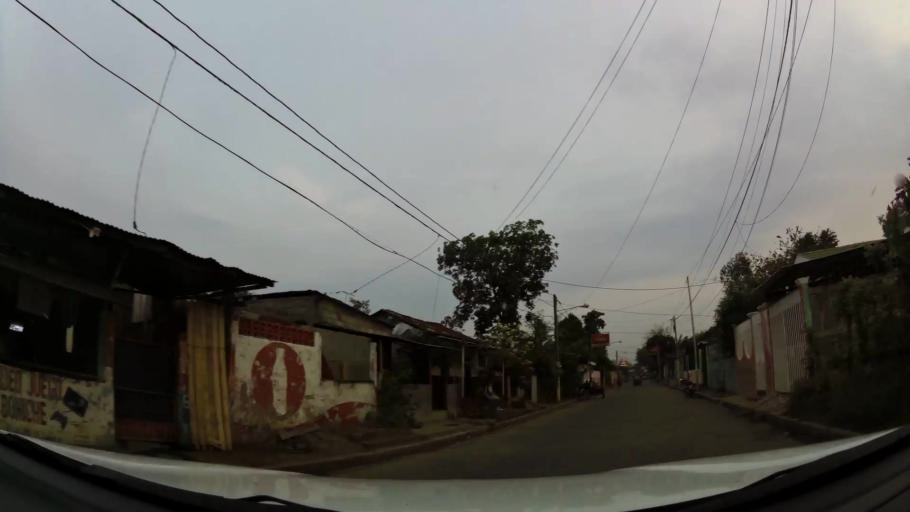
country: NI
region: Masaya
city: Nindiri
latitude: 12.0064
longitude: -86.1197
